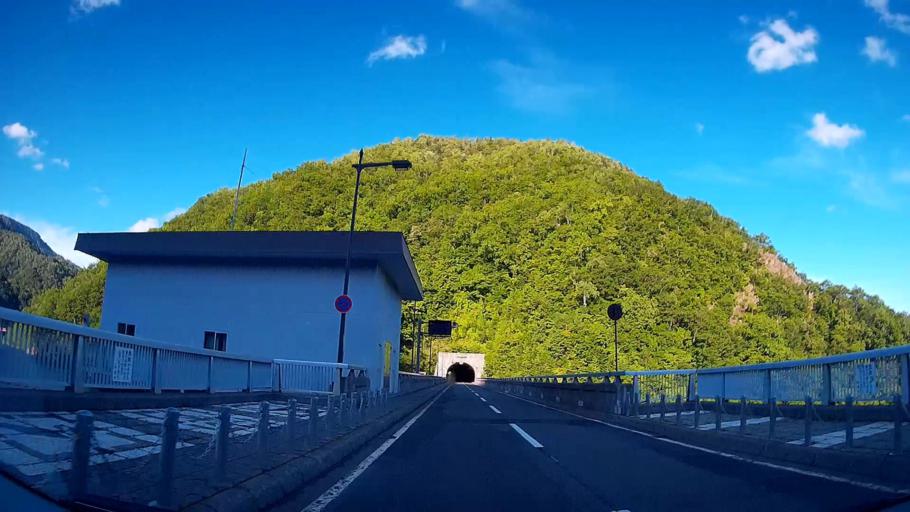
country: JP
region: Hokkaido
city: Sapporo
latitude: 42.9849
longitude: 141.1578
